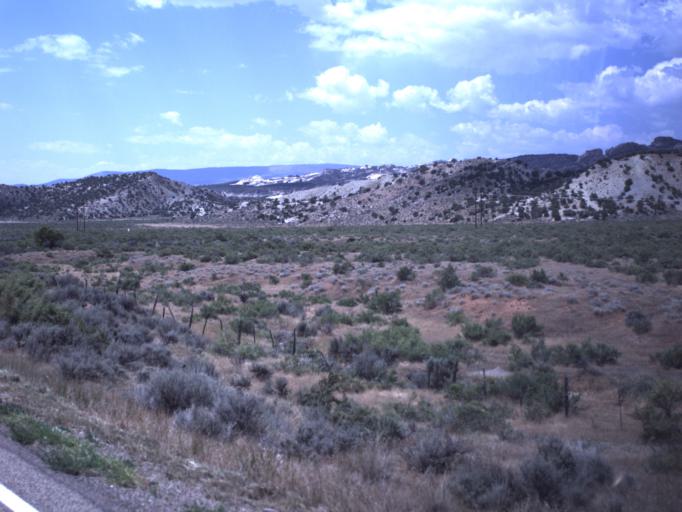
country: US
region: Utah
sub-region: Uintah County
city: Vernal
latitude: 40.5517
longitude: -109.5207
